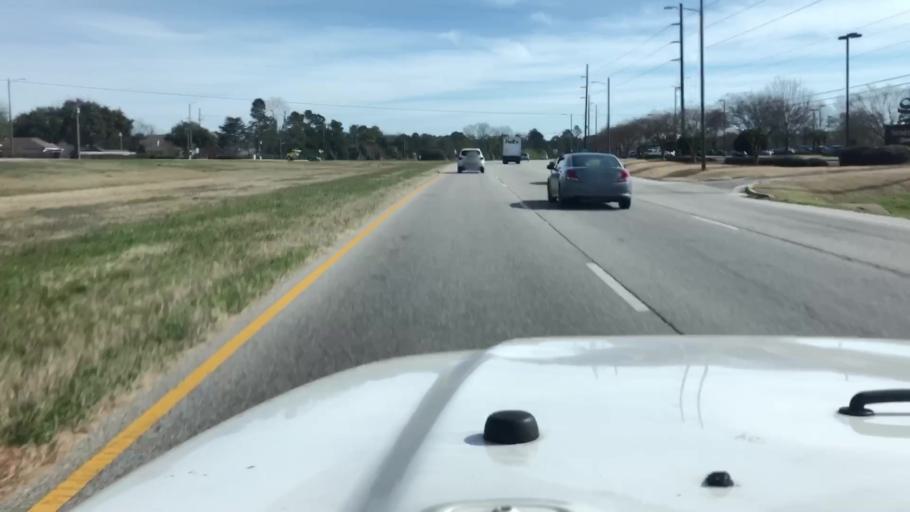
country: US
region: Alabama
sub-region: Elmore County
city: Blue Ridge
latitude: 32.3819
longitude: -86.1637
